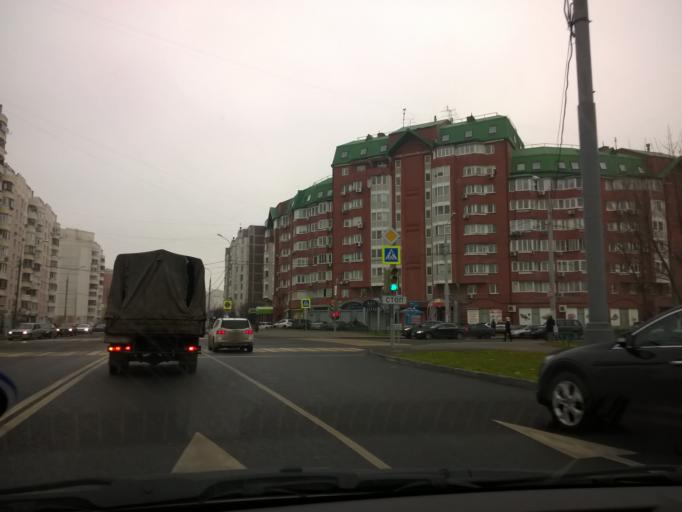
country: RU
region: Moskovskaya
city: Kommunarka
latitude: 55.5338
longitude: 37.5163
